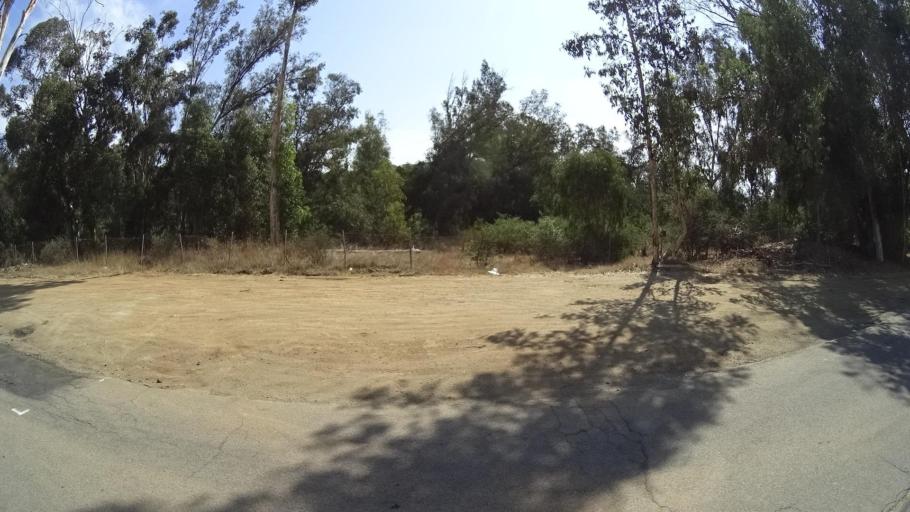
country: US
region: California
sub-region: San Diego County
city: San Marcos
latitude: 33.2005
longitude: -117.1672
